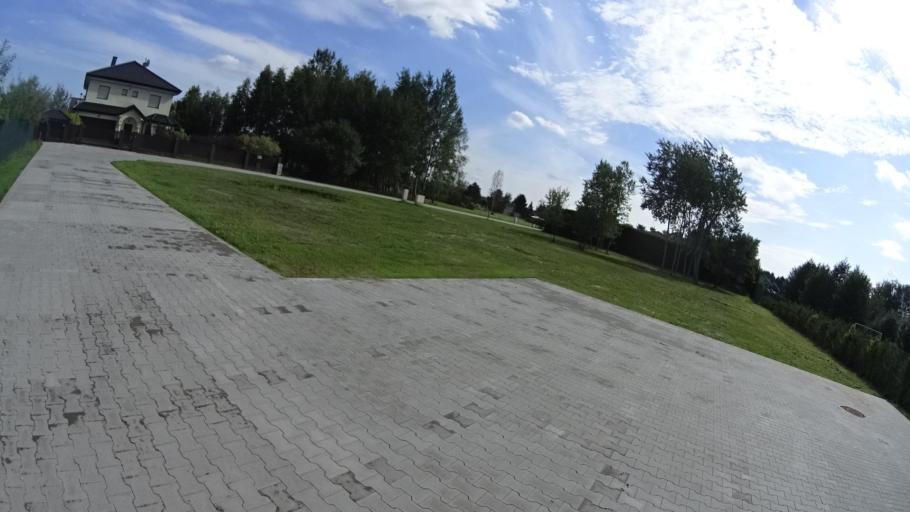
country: PL
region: Masovian Voivodeship
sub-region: Powiat piaseczynski
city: Lesznowola
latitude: 52.0683
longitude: 20.9395
